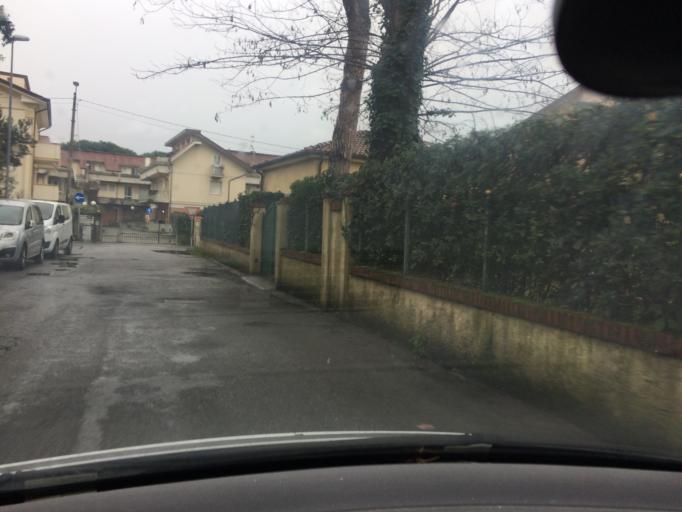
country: IT
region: Tuscany
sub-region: Provincia di Massa-Carrara
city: Massa
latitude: 44.0150
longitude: 10.0946
